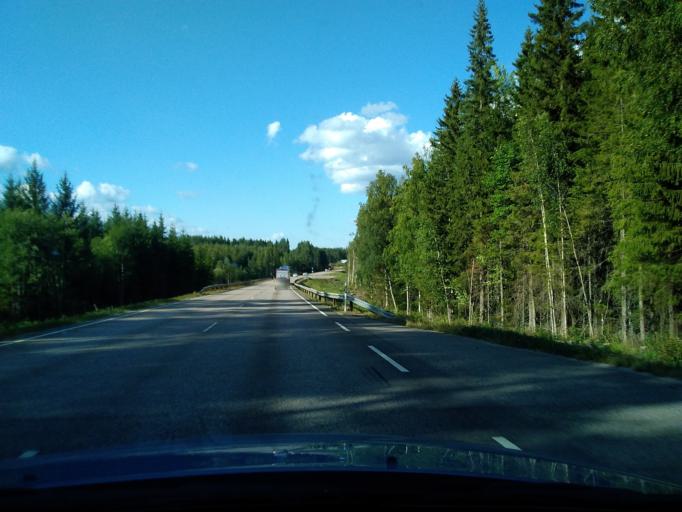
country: FI
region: Pirkanmaa
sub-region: Ylae-Pirkanmaa
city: Maenttae
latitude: 62.0919
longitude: 24.7279
